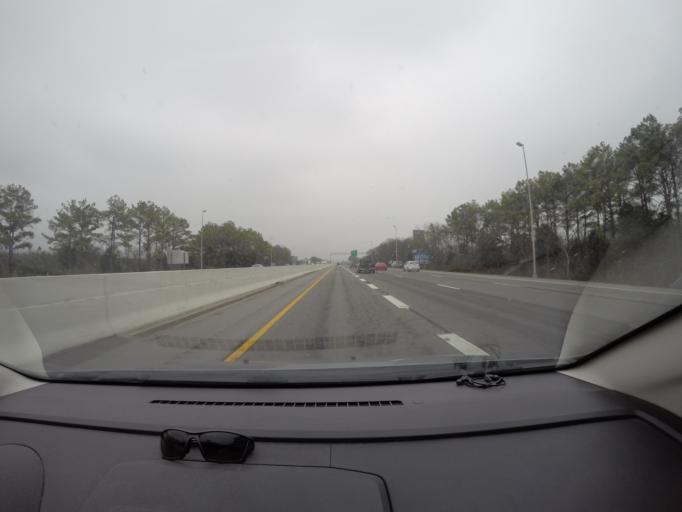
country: US
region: Tennessee
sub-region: Rutherford County
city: Murfreesboro
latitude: 35.8373
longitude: -86.4243
